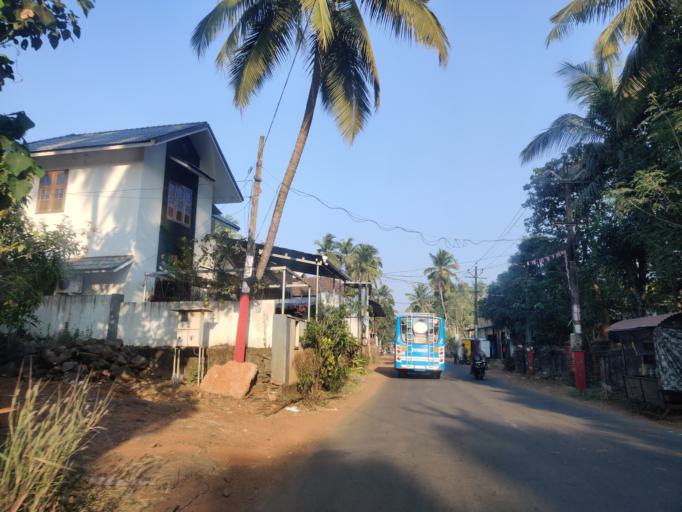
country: IN
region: Kerala
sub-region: Thrissur District
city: Kunnamkulam
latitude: 10.7347
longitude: 76.0229
